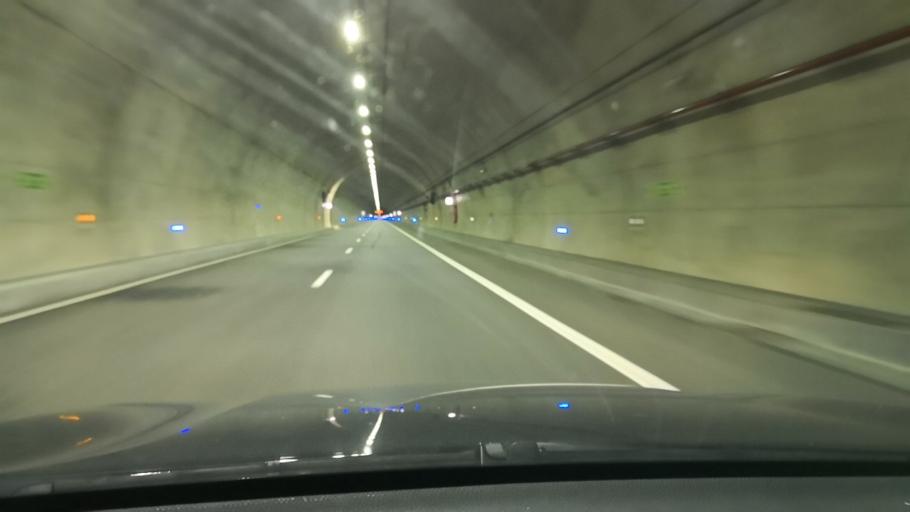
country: PT
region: Vila Real
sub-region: Mesao Frio
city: Mesao Frio
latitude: 41.2694
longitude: -7.9271
